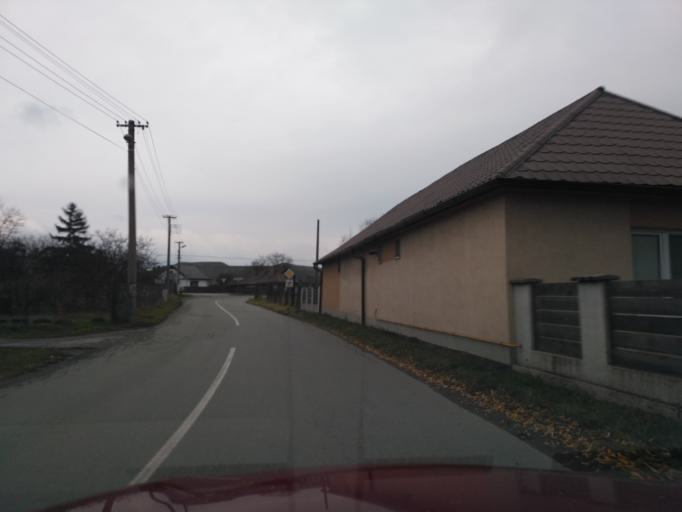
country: SK
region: Kosicky
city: Kosice
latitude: 48.5929
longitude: 21.1678
